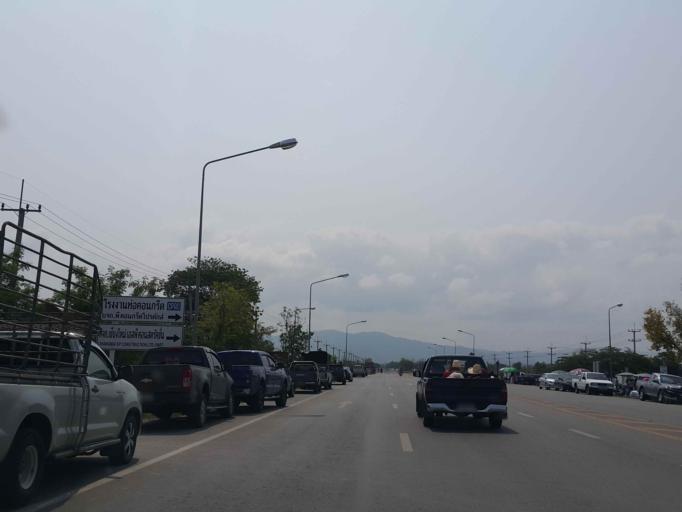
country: TH
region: Chiang Mai
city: San Kamphaeng
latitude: 18.7206
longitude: 99.1114
